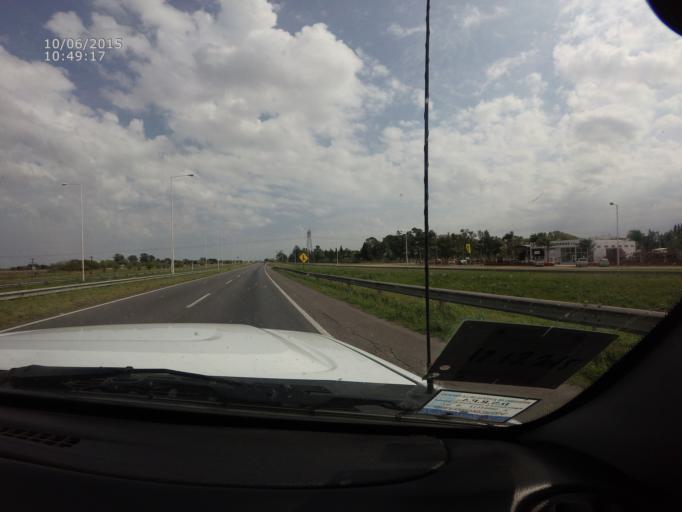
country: AR
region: Buenos Aires
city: San Nicolas de los Arroyos
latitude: -33.3869
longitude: -60.2238
